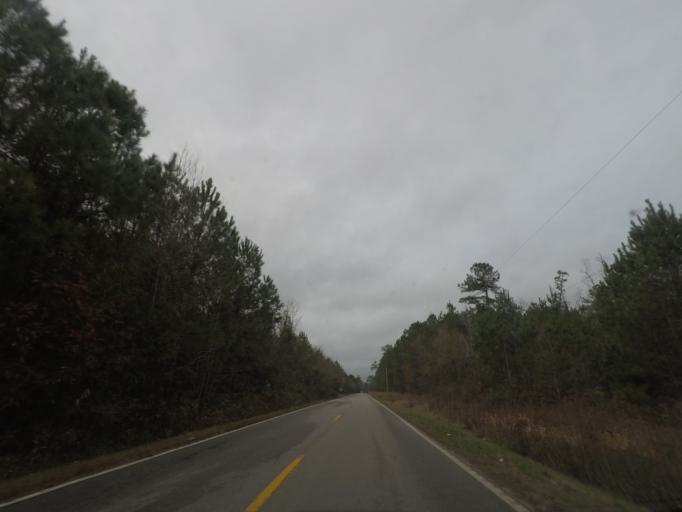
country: US
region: South Carolina
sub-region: Colleton County
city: Walterboro
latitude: 32.8740
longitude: -80.4903
